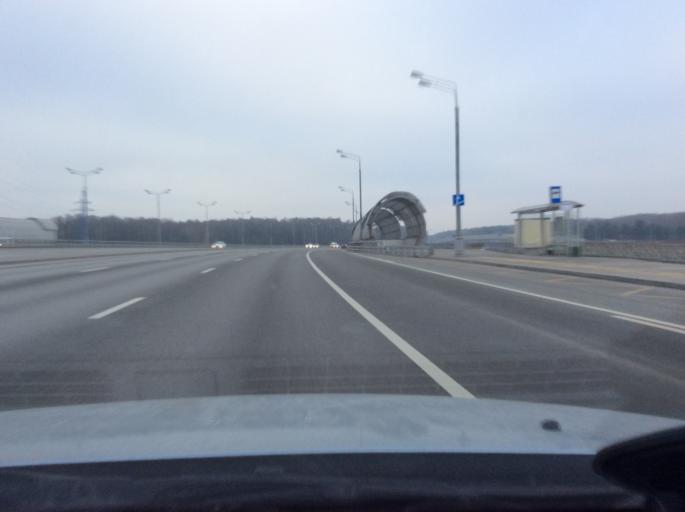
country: RU
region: Moskovskaya
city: Kommunarka
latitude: 55.5511
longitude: 37.4330
